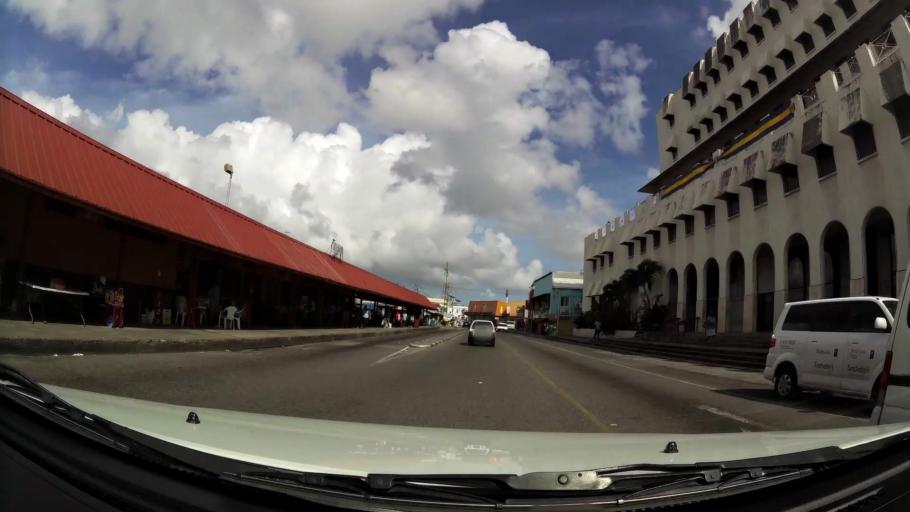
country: BB
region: Saint Michael
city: Bridgetown
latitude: 13.0957
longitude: -59.6125
